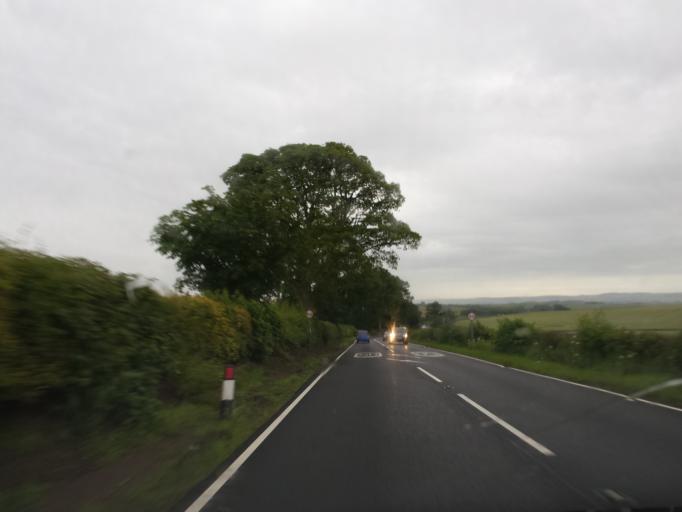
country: GB
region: Scotland
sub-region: Fife
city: Newport-On-Tay
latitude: 56.4252
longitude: -2.9239
